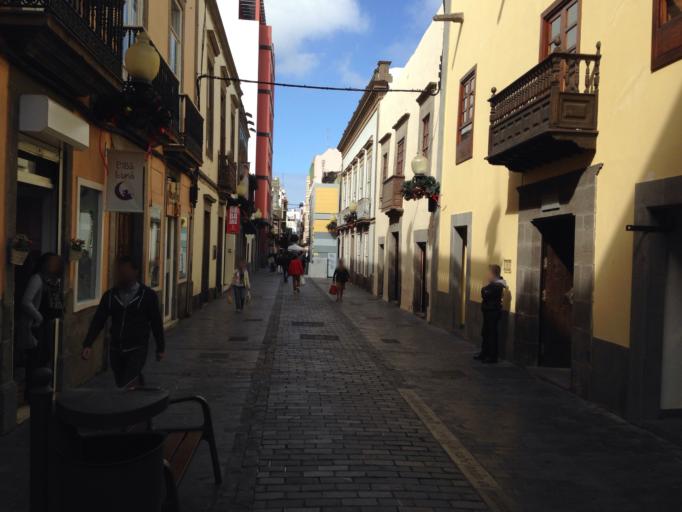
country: ES
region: Canary Islands
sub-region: Provincia de Las Palmas
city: Las Palmas de Gran Canaria
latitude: 28.1040
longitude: -15.4160
